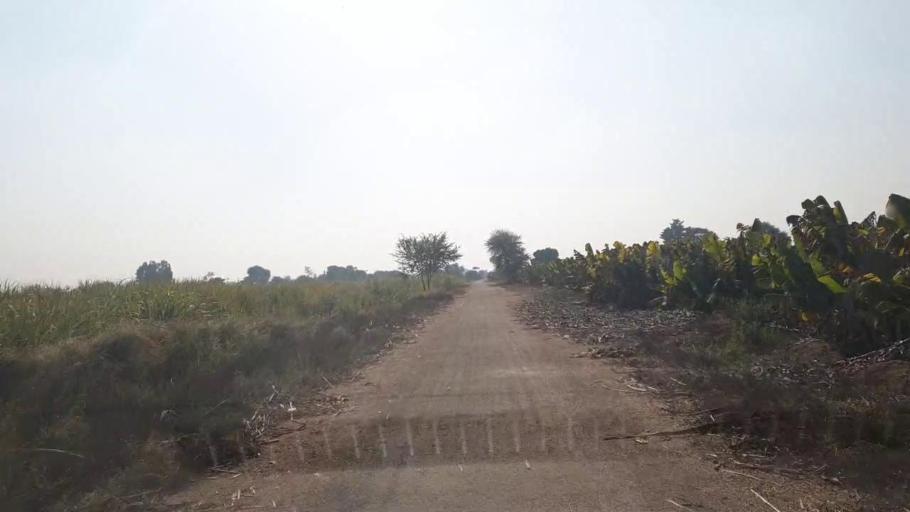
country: PK
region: Sindh
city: Shahdadpur
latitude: 25.9701
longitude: 68.5403
